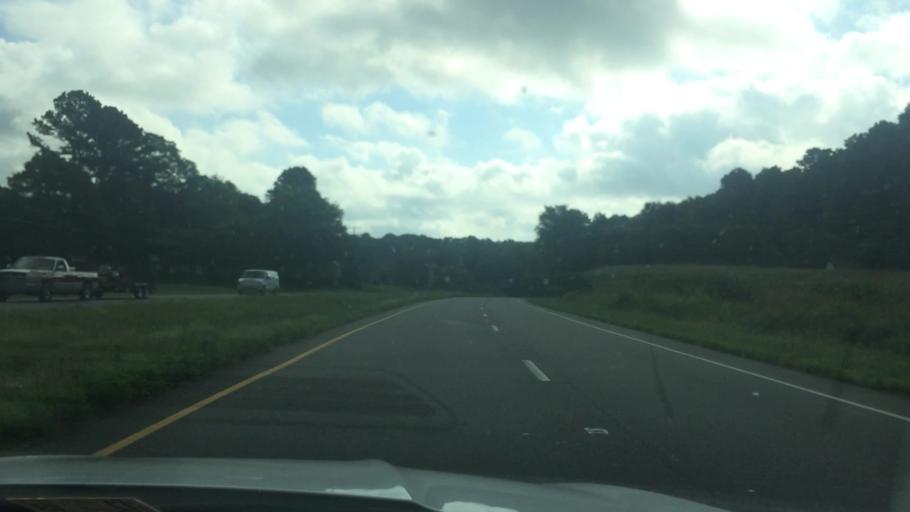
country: US
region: Virginia
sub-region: Gloucester County
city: Gloucester Courthouse
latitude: 37.4257
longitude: -76.5021
